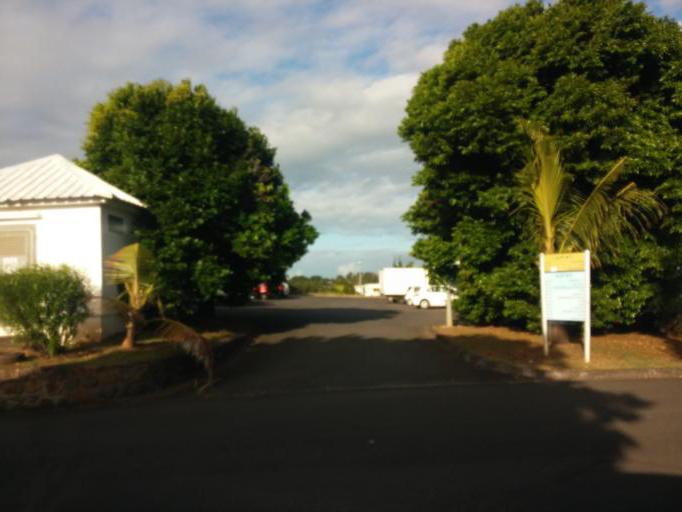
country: RE
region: Reunion
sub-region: Reunion
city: Sainte-Marie
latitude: -20.9001
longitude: 55.5297
